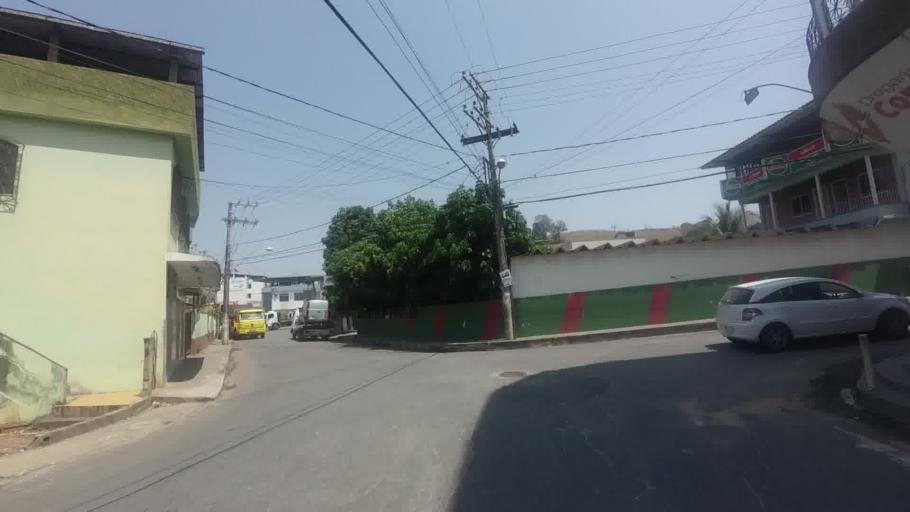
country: BR
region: Espirito Santo
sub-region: Cachoeiro De Itapemirim
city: Cachoeiro de Itapemirim
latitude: -20.8530
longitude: -41.0965
